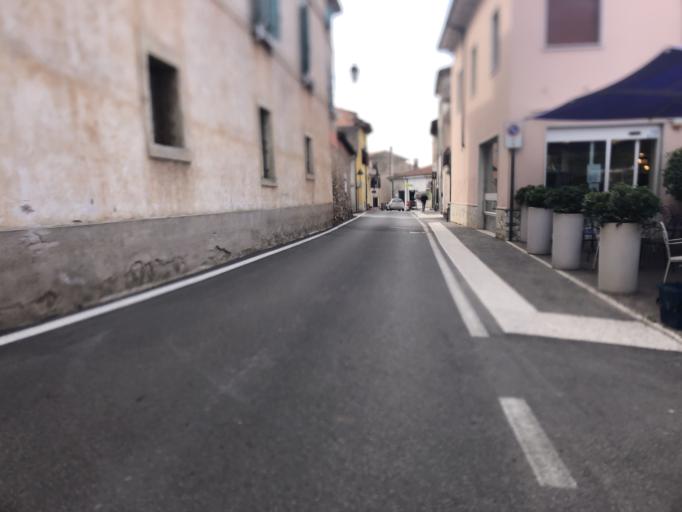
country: IT
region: Veneto
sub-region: Provincia di Verona
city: San Giorgio in Salici
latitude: 45.4270
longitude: 10.7879
